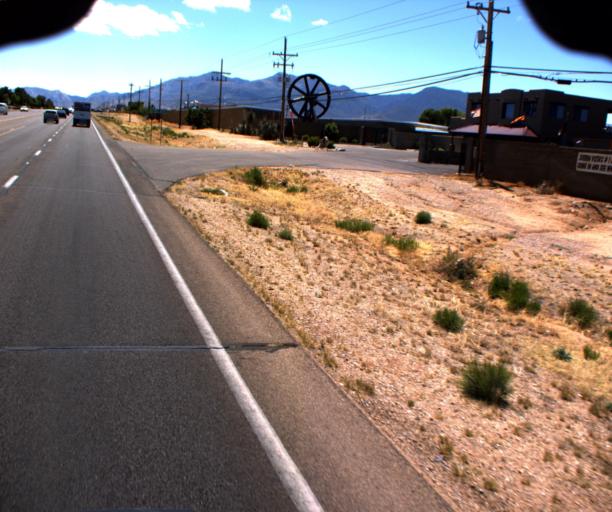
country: US
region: Arizona
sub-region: Cochise County
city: Sierra Vista
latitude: 31.5421
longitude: -110.2574
